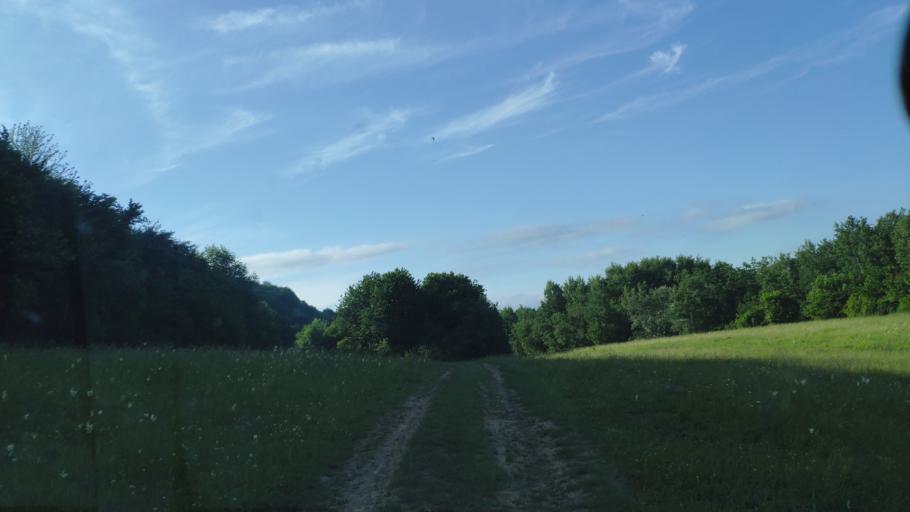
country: SK
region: Presovsky
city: Vranov nad Topl'ou
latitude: 48.8178
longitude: 21.5899
